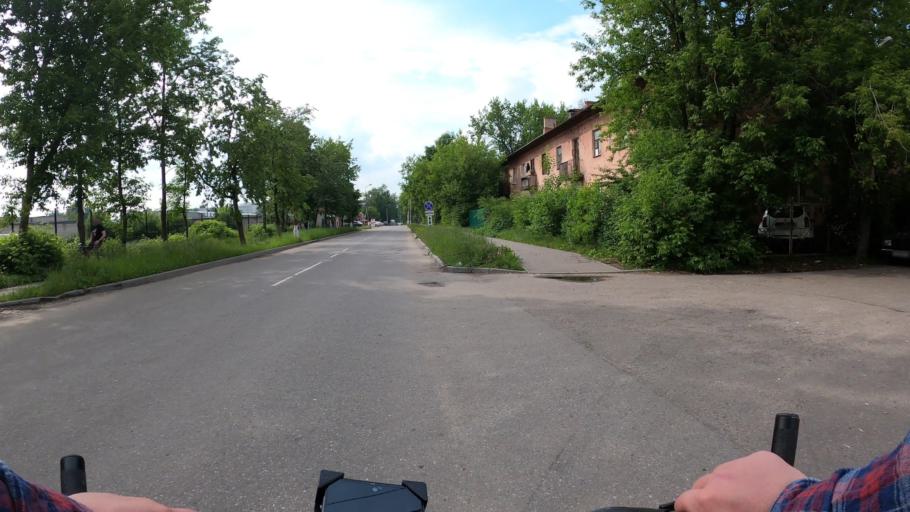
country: RU
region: Moskovskaya
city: Zhukovskiy
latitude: 55.6053
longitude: 38.1114
